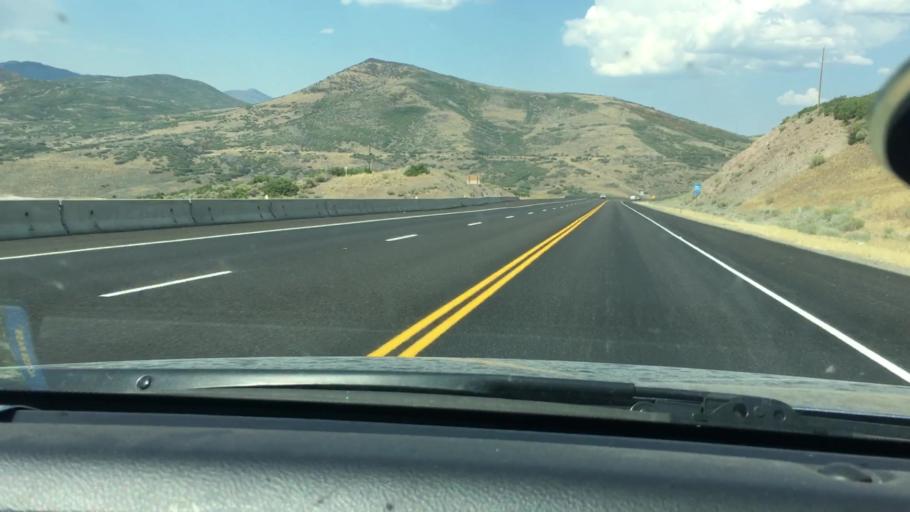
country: US
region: Utah
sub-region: Summit County
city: Park City
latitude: 40.6512
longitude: -111.4068
